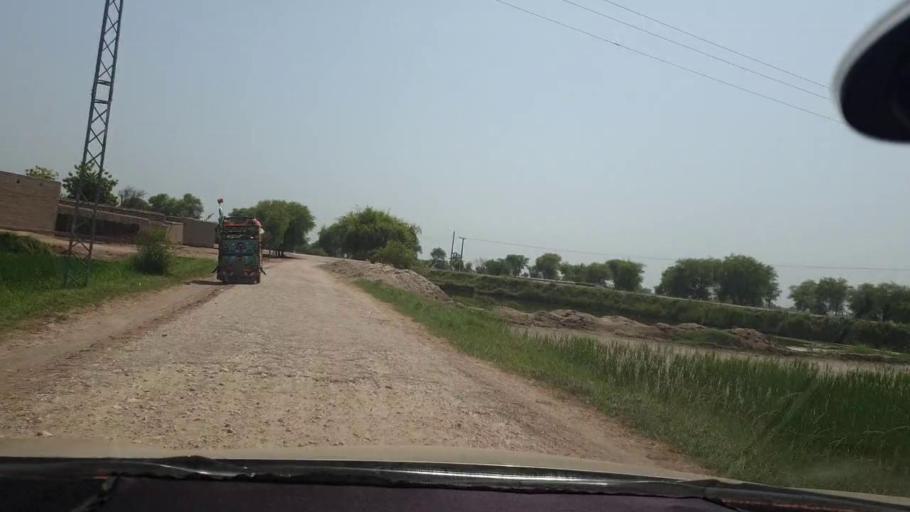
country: PK
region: Sindh
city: Kambar
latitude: 27.6286
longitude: 67.9341
